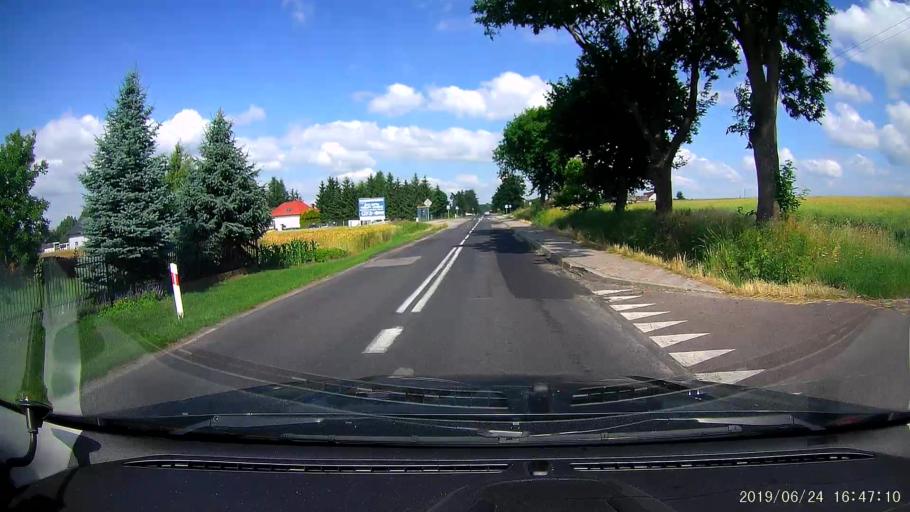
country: PL
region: Lublin Voivodeship
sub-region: Powiat tomaszowski
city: Laszczow
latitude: 50.5296
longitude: 23.6951
